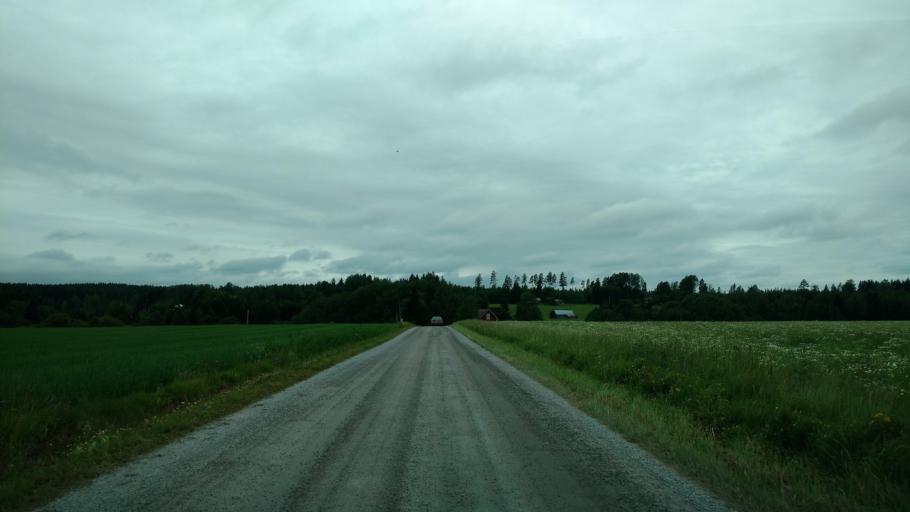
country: FI
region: Varsinais-Suomi
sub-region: Salo
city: Halikko
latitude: 60.4789
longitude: 23.0065
